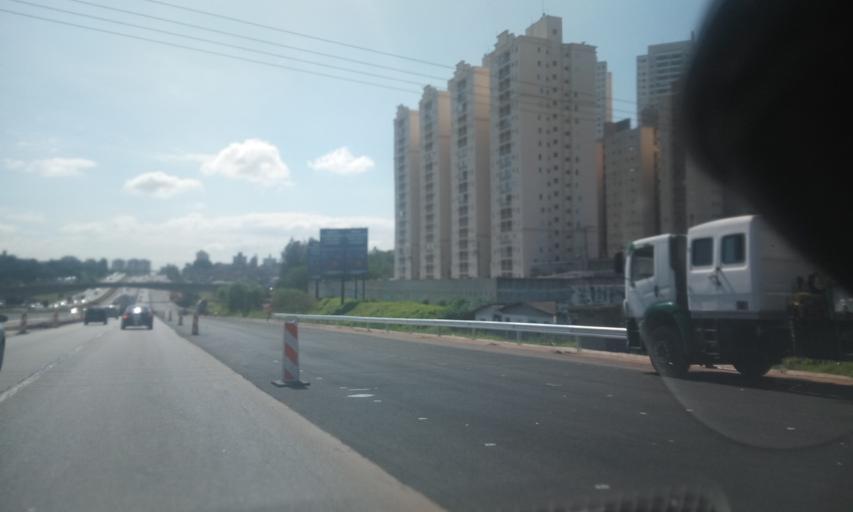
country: BR
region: Sao Paulo
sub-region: Sao Bernardo Do Campo
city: Sao Bernardo do Campo
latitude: -23.7125
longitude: -46.5611
